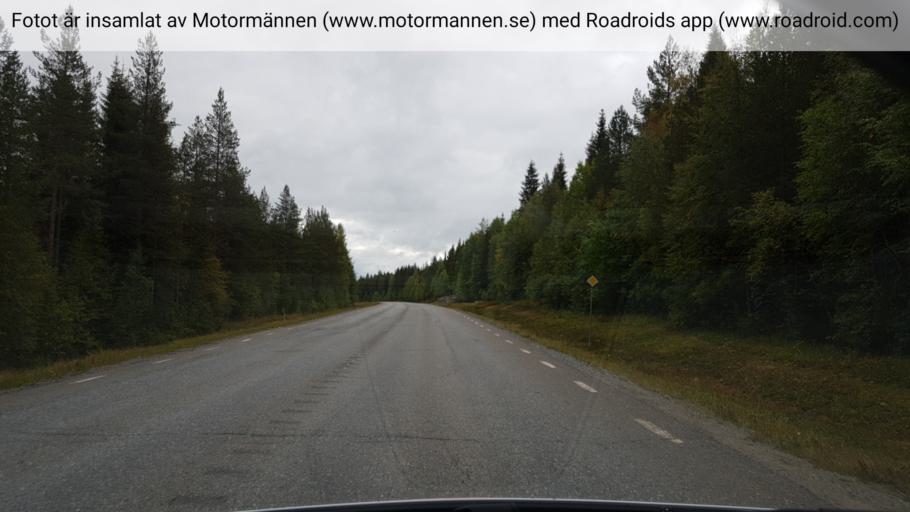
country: SE
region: Vaesterbotten
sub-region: Skelleftea Kommun
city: Boliden
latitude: 64.8903
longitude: 20.3773
